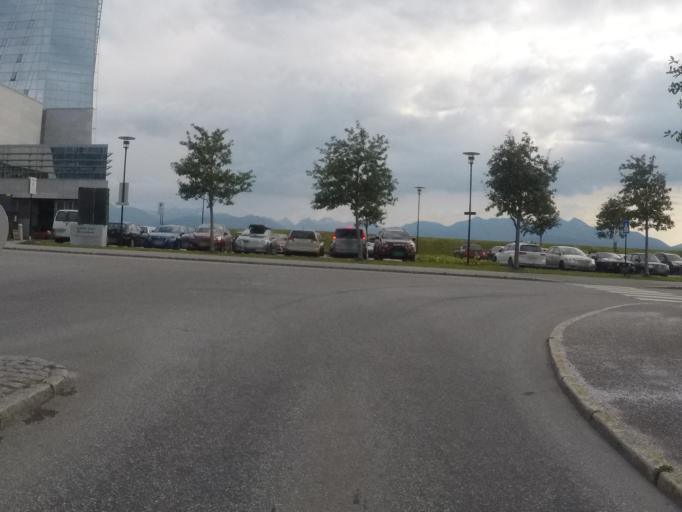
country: NO
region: More og Romsdal
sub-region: Molde
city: Molde
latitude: 62.7337
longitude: 7.1431
